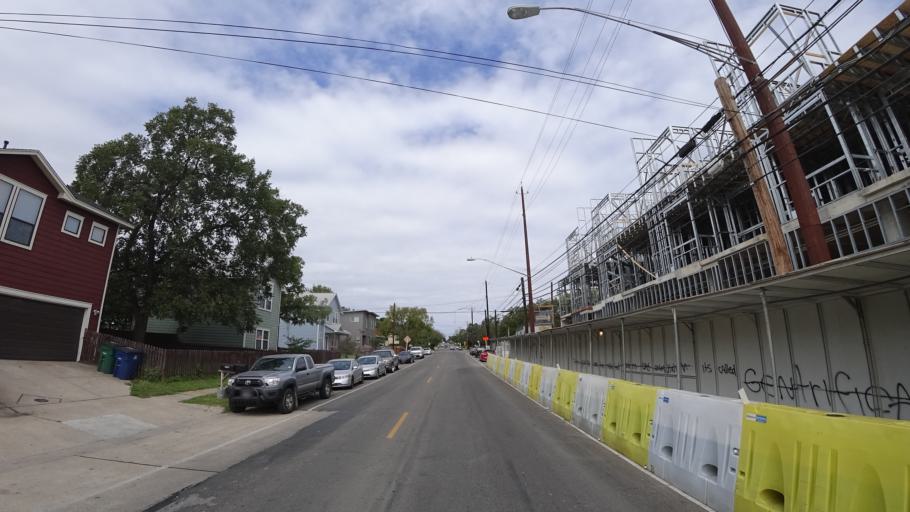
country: US
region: Texas
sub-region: Travis County
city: Austin
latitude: 30.2750
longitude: -97.7201
